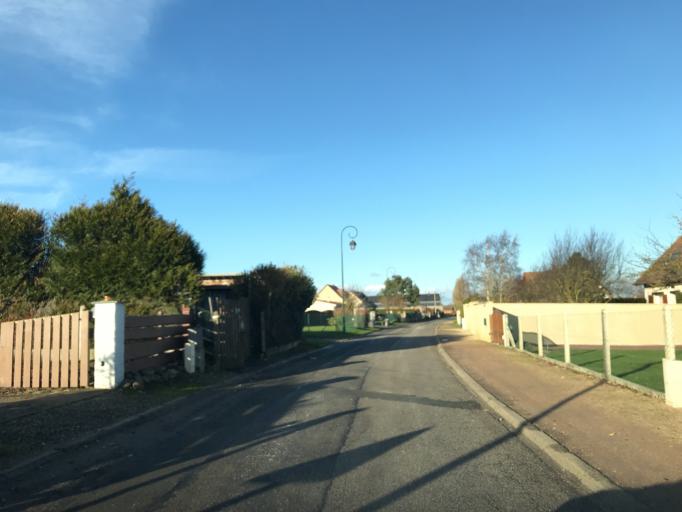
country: FR
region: Haute-Normandie
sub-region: Departement de l'Eure
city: Gravigny
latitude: 49.0792
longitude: 1.2229
